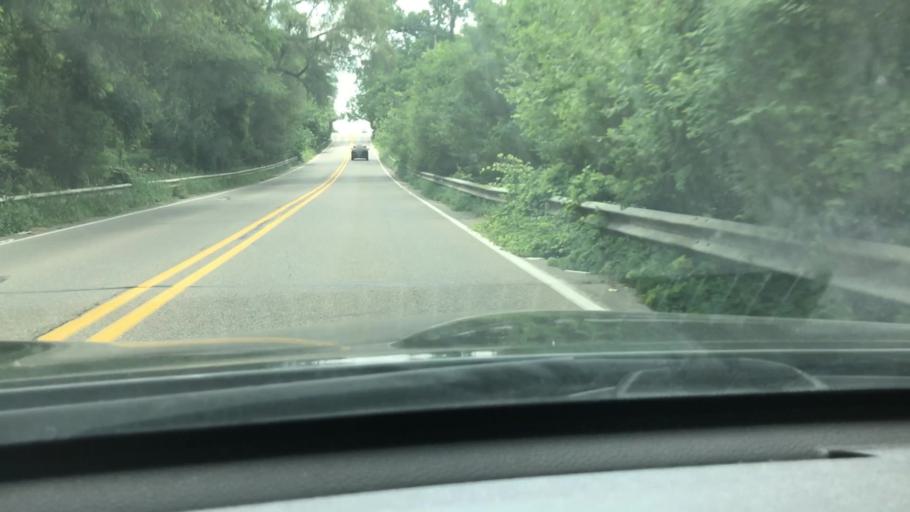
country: US
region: Michigan
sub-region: Wayne County
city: Northville
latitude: 42.4057
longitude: -83.4821
